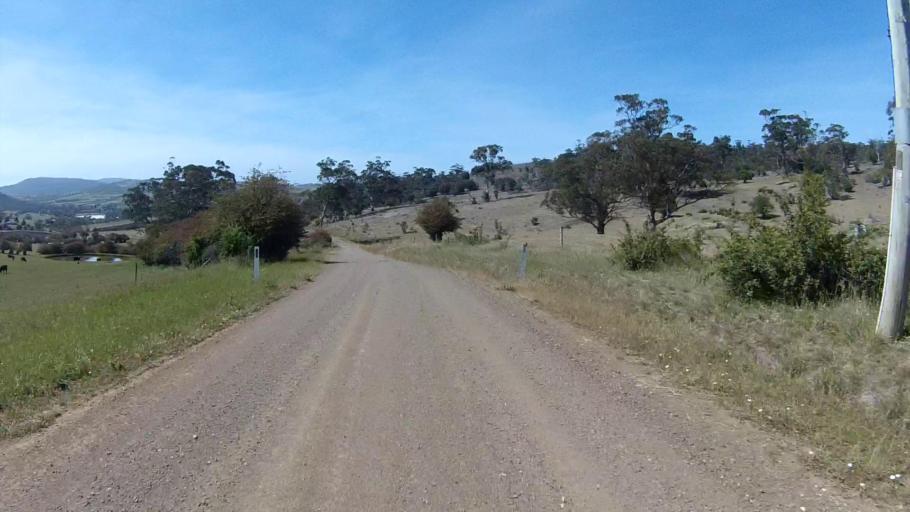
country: AU
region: Tasmania
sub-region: Sorell
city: Sorell
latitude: -42.7424
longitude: 147.6004
